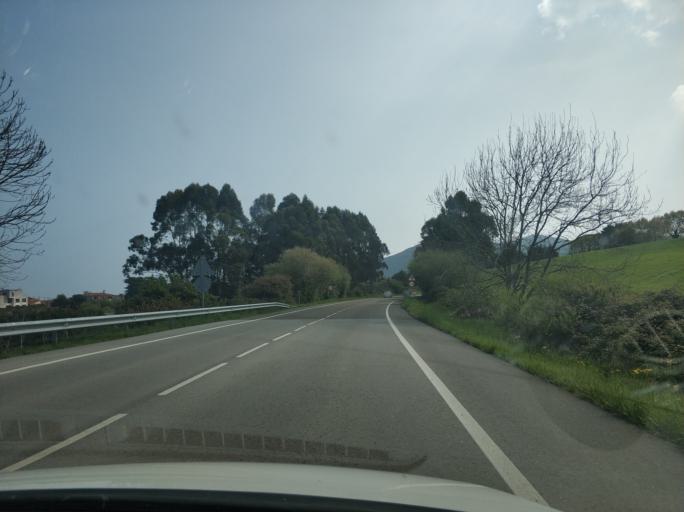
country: ES
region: Cantabria
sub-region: Provincia de Cantabria
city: Argonos
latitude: 43.4613
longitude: -3.4773
